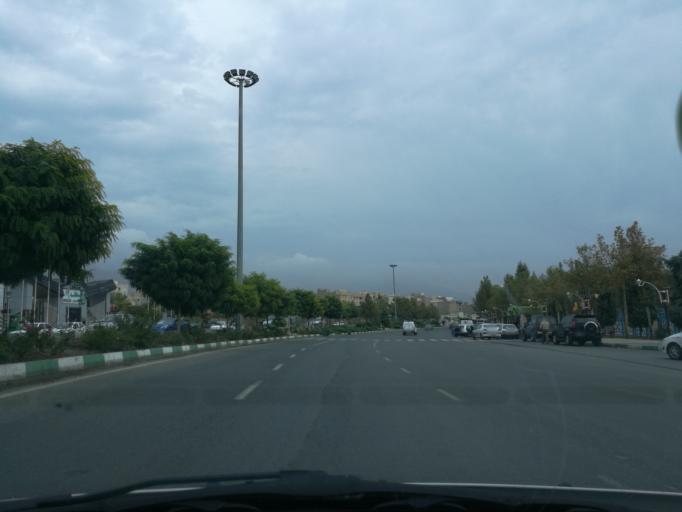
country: IR
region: Alborz
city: Karaj
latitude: 35.8518
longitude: 50.9652
